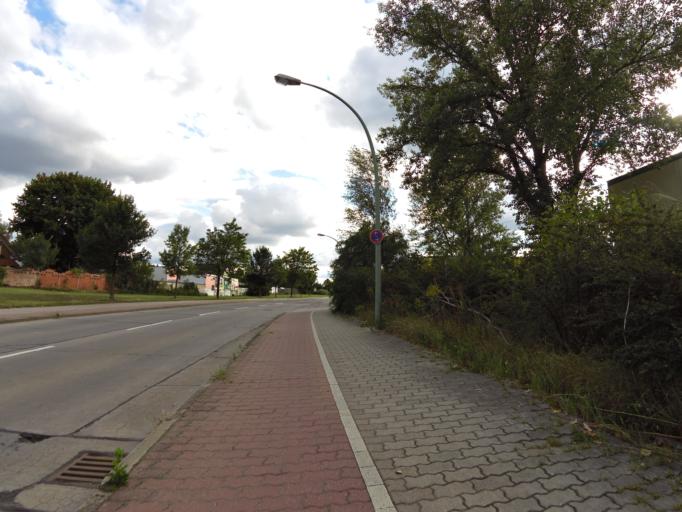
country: DE
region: Berlin
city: Altglienicke
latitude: 52.4220
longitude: 13.5254
